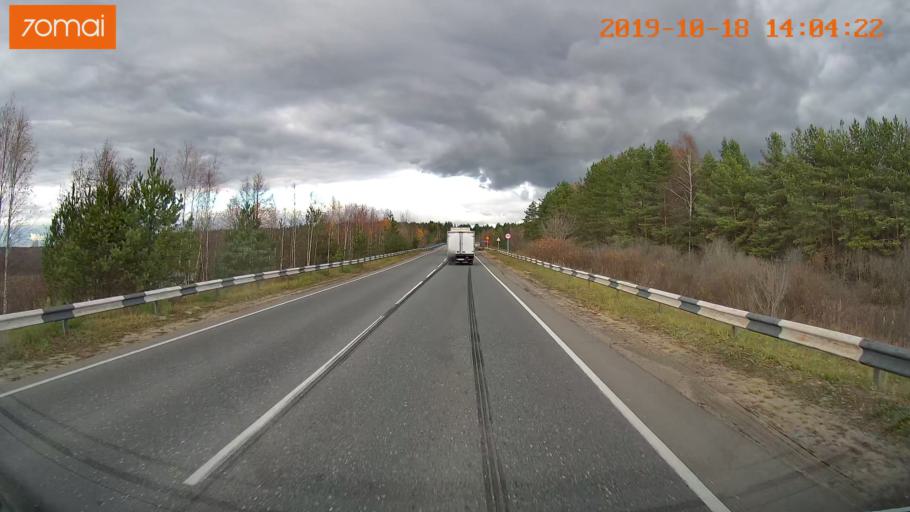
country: RU
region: Rjazan
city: Spas-Klepiki
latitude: 55.1252
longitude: 40.1335
